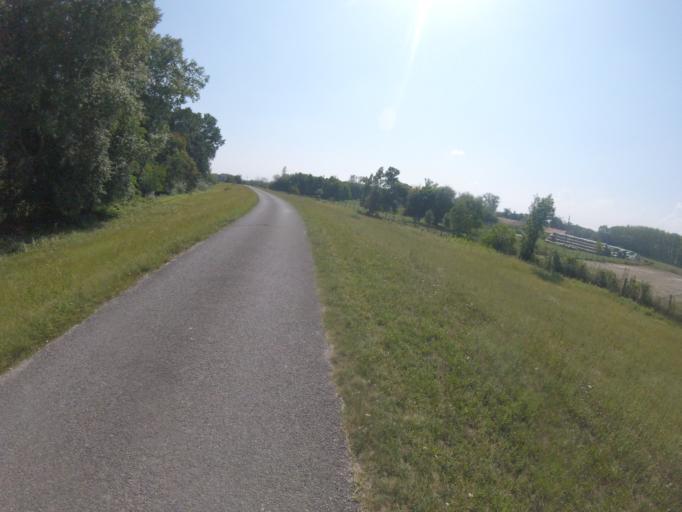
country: HU
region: Tolna
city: Bata
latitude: 46.2073
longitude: 18.8211
